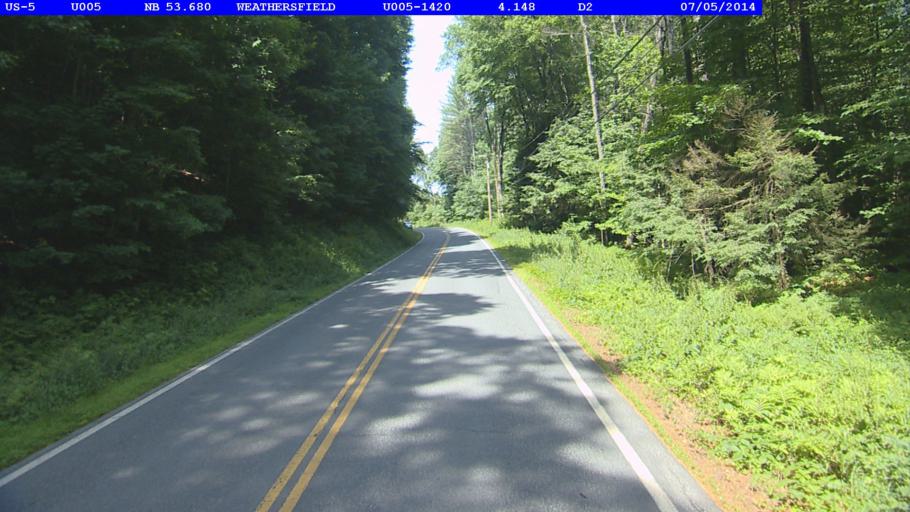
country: US
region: New Hampshire
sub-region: Sullivan County
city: Claremont
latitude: 43.3922
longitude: -72.4059
